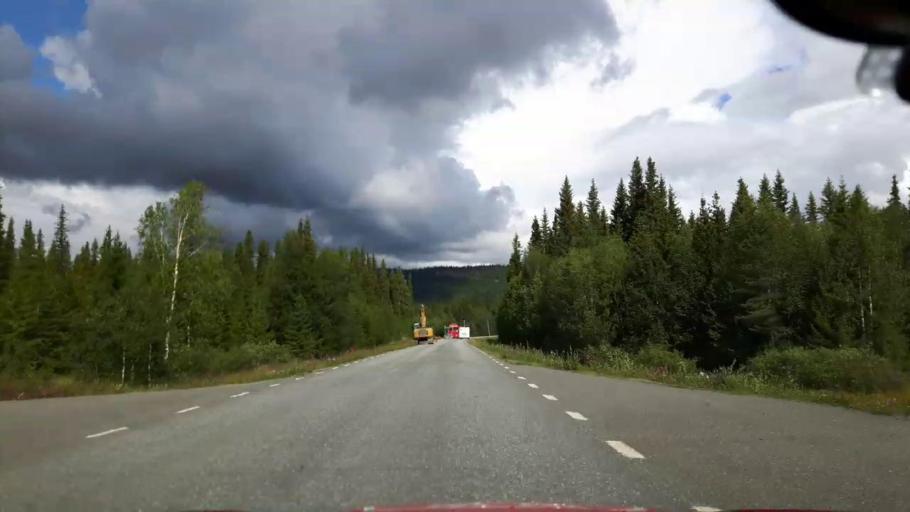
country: SE
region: Vaesterbotten
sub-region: Vilhelmina Kommun
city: Sjoberg
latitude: 64.9313
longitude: 15.8602
